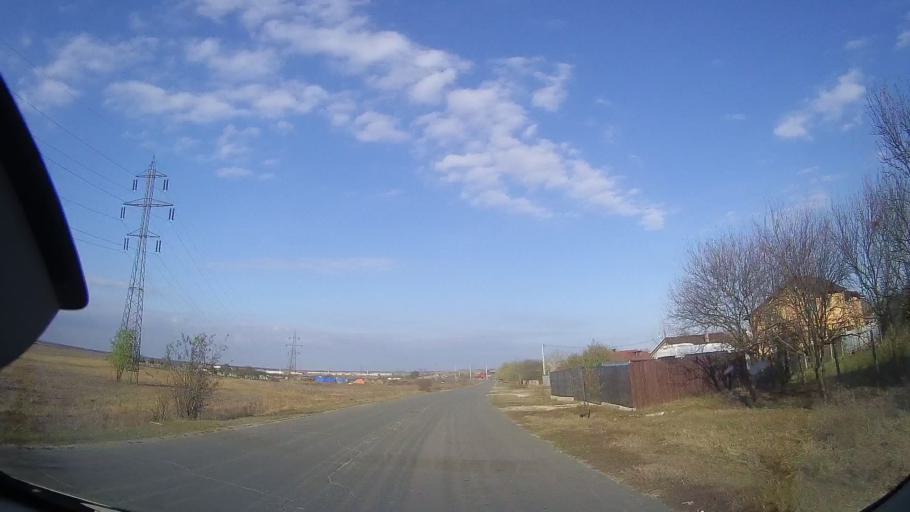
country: RO
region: Constanta
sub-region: Comuna Limanu
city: Limanu
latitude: 43.7968
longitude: 28.5201
